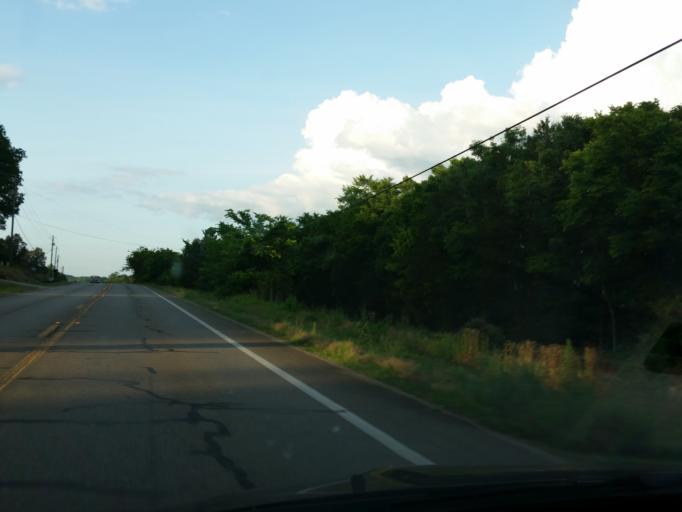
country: US
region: Georgia
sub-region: Walker County
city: Chattanooga Valley
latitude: 34.9434
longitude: -85.4470
